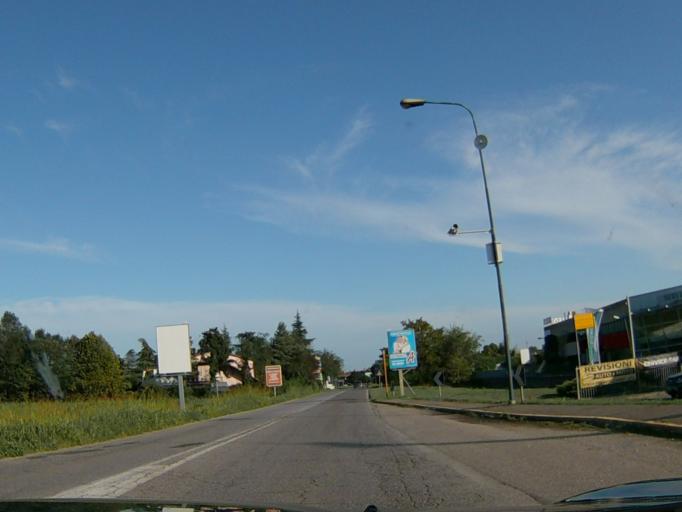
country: IT
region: Lombardy
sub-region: Provincia di Brescia
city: Molinetto
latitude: 45.4887
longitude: 10.3672
